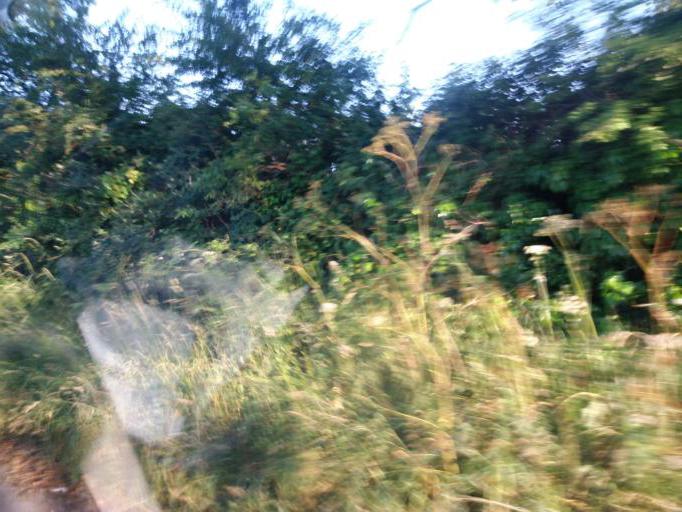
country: IE
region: Leinster
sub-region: An Mhi
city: Ashbourne
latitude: 53.5755
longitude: -6.3598
